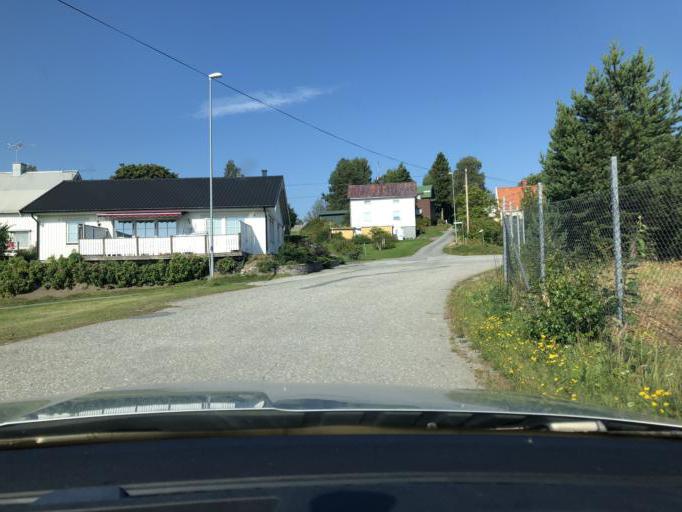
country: SE
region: Vaesternorrland
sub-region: Kramfors Kommun
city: Kramfors
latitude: 62.8798
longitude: 17.8734
